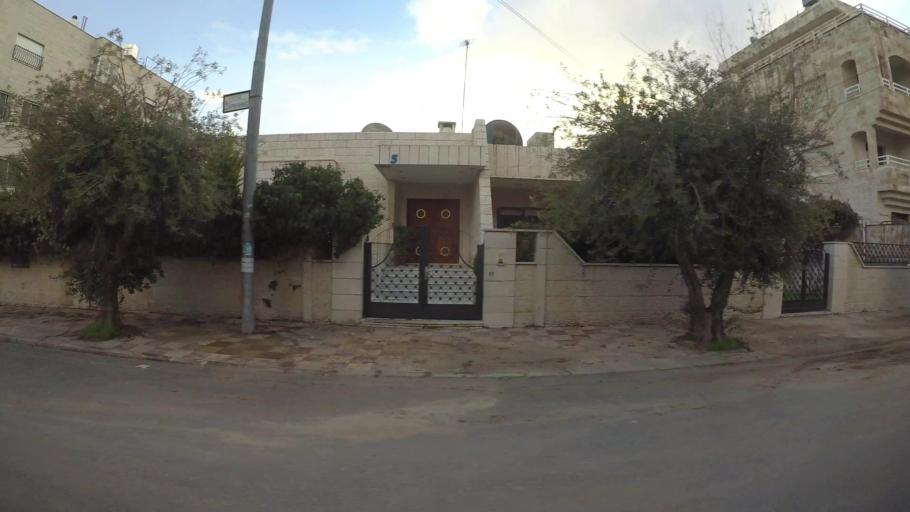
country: JO
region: Amman
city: Al Jubayhah
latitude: 31.9835
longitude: 35.8635
